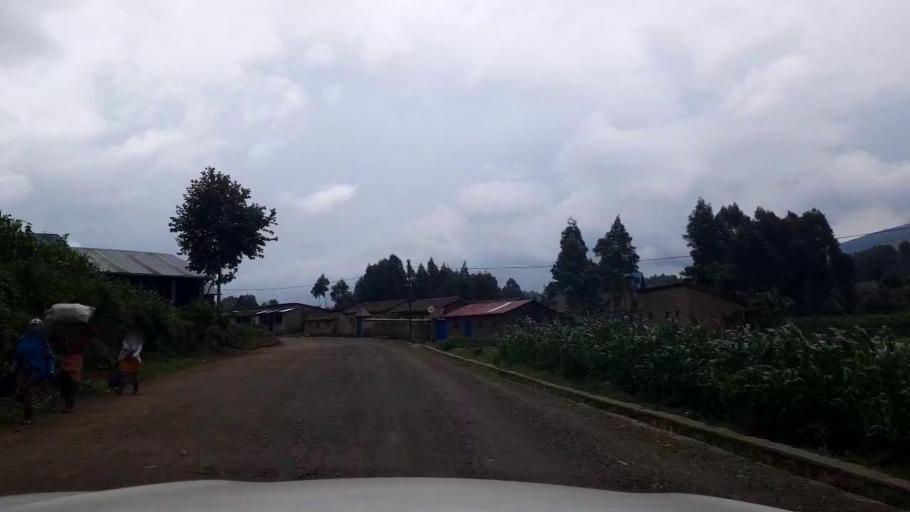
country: RW
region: Northern Province
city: Musanze
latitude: -1.5812
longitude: 29.4806
